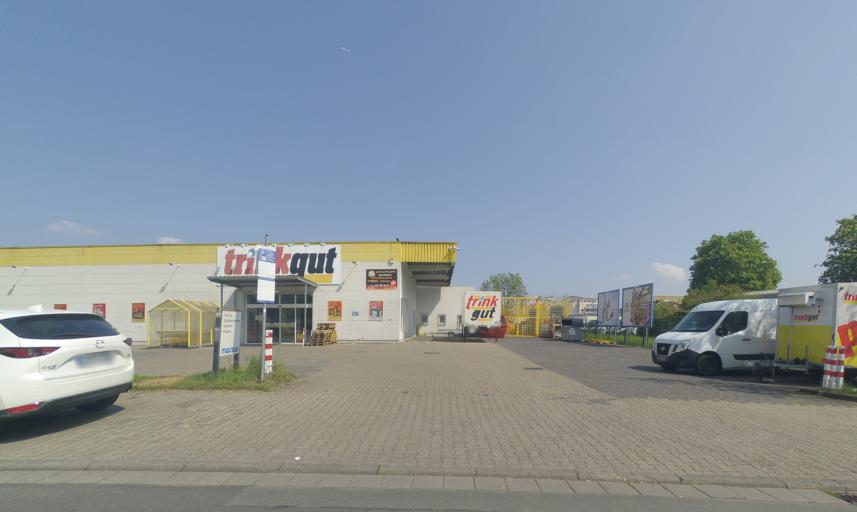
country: DE
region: Hesse
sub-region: Regierungsbezirk Darmstadt
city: Offenbach
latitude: 50.0869
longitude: 8.7488
